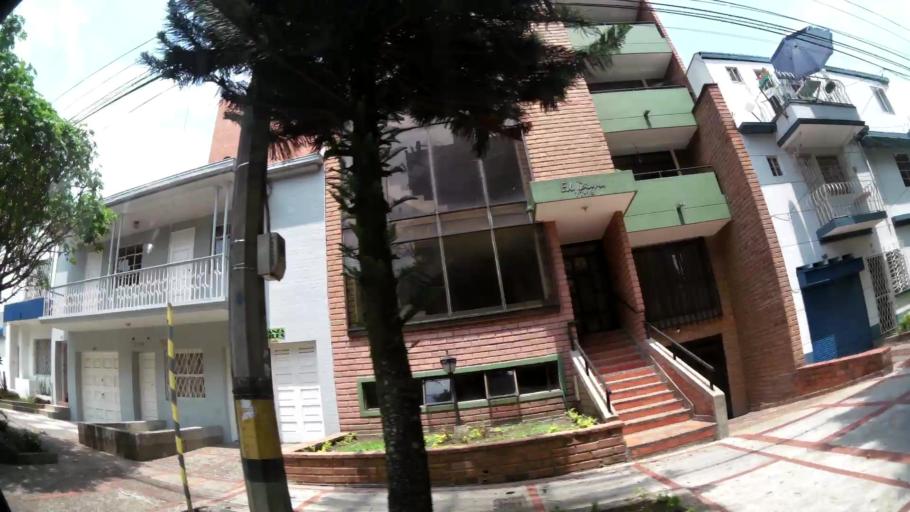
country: CO
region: Antioquia
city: Medellin
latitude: 6.2454
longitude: -75.5990
